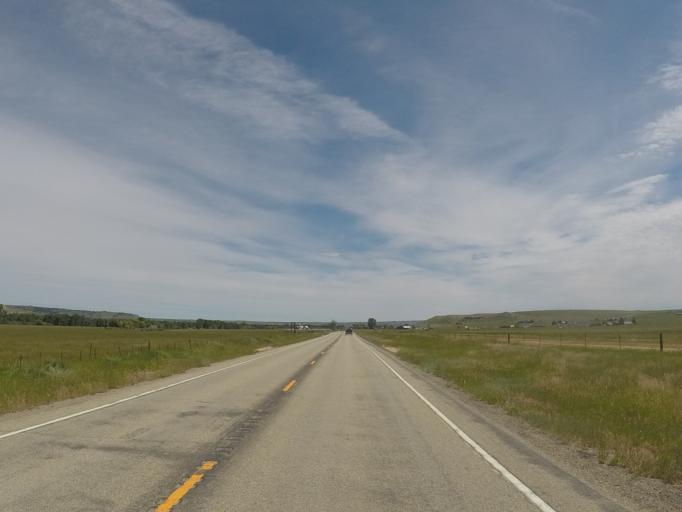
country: US
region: Montana
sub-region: Stillwater County
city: Columbus
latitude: 45.4266
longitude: -109.1025
